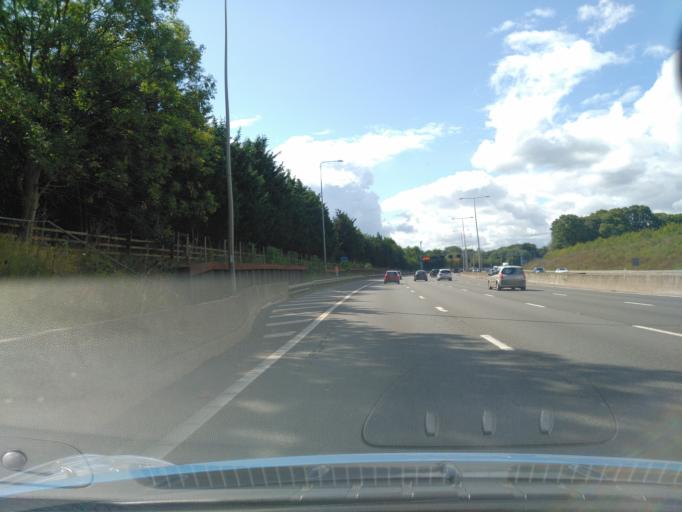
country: GB
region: England
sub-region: Hertfordshire
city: Chorleywood
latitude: 51.6753
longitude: -0.4614
